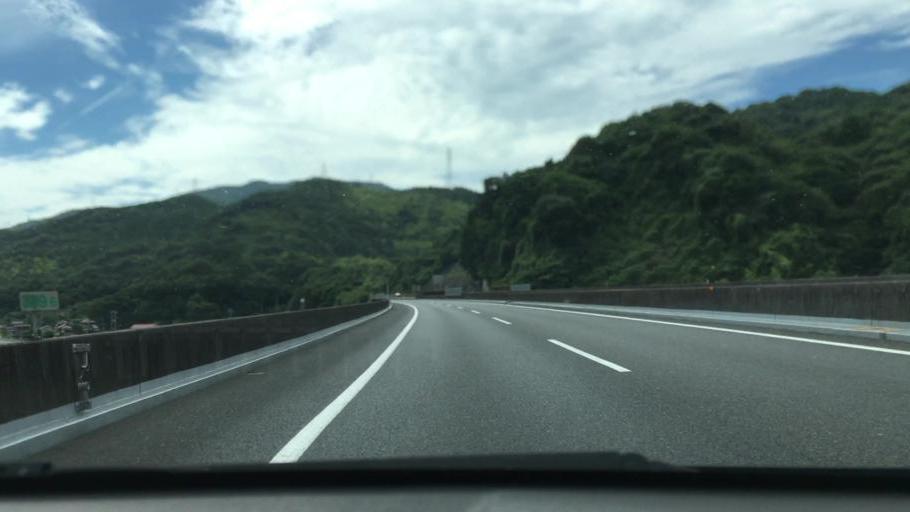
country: JP
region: Yamaguchi
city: Hofu
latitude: 34.0723
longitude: 131.6786
